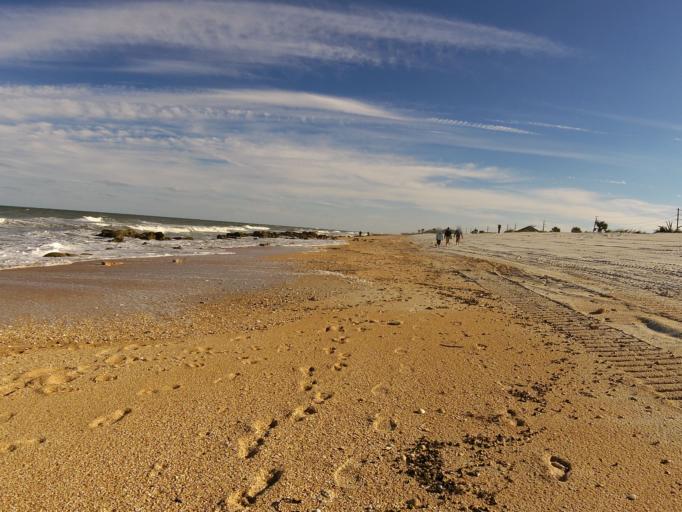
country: US
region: Florida
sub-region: Flagler County
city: Palm Coast
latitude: 29.6634
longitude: -81.2101
